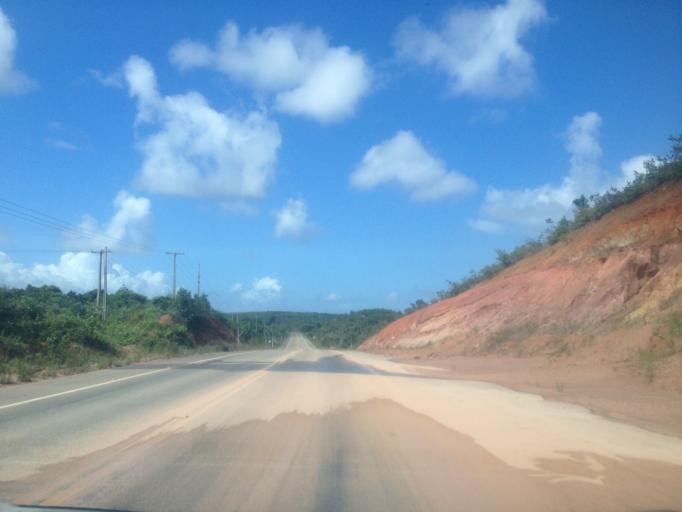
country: BR
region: Sergipe
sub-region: Indiaroba
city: Indiaroba
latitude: -11.4865
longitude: -37.4820
